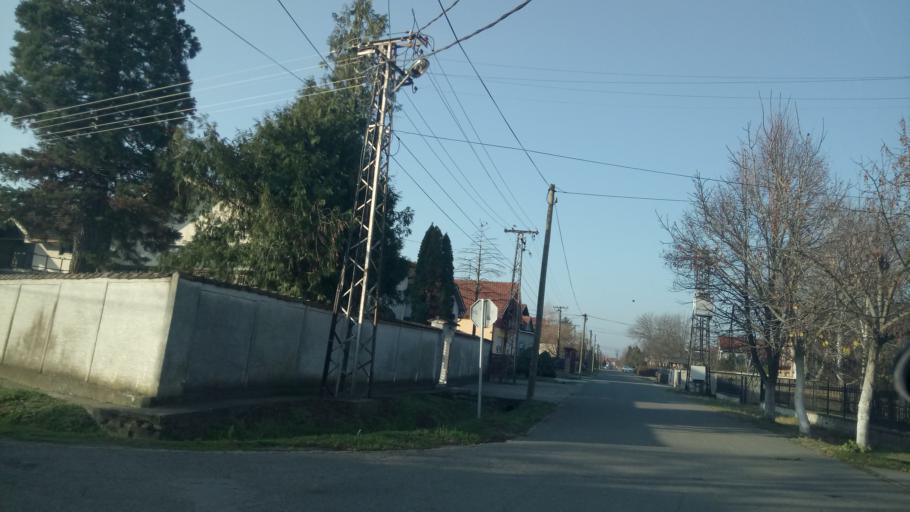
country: RS
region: Autonomna Pokrajina Vojvodina
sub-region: Sremski Okrug
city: Stara Pazova
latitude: 44.9854
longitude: 20.1831
